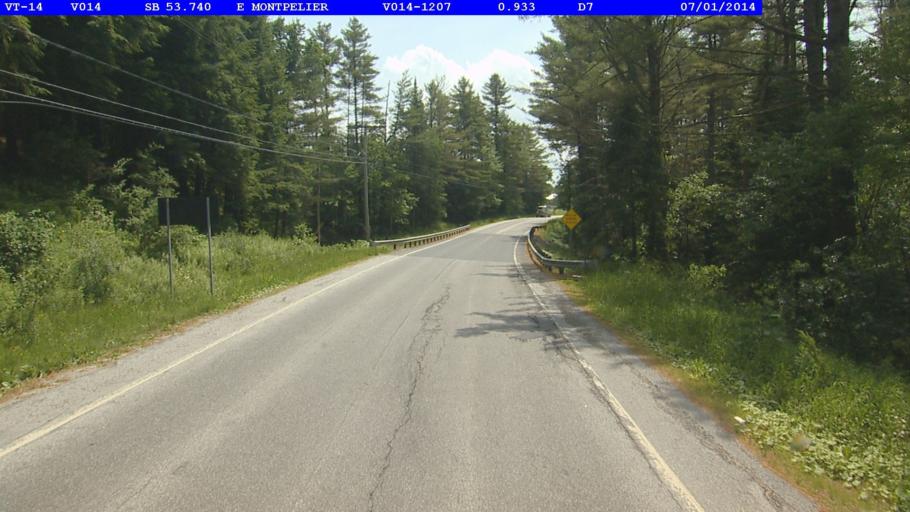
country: US
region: Vermont
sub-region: Washington County
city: Barre
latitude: 44.2484
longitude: -72.4867
